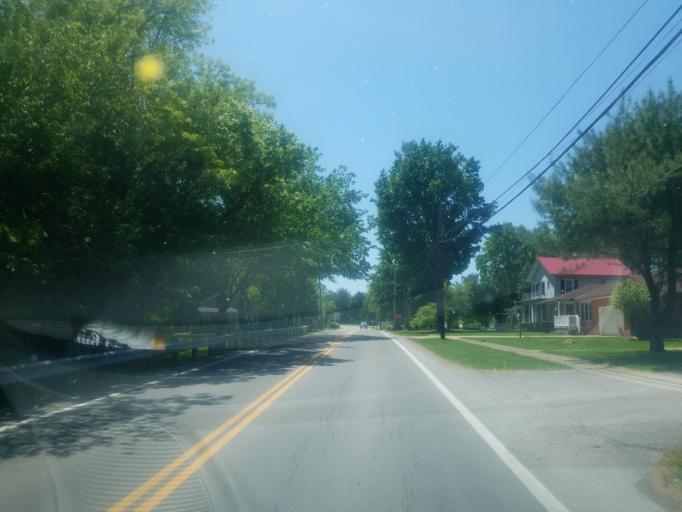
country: US
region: Ohio
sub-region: Huron County
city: Wakeman
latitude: 41.2542
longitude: -82.3997
